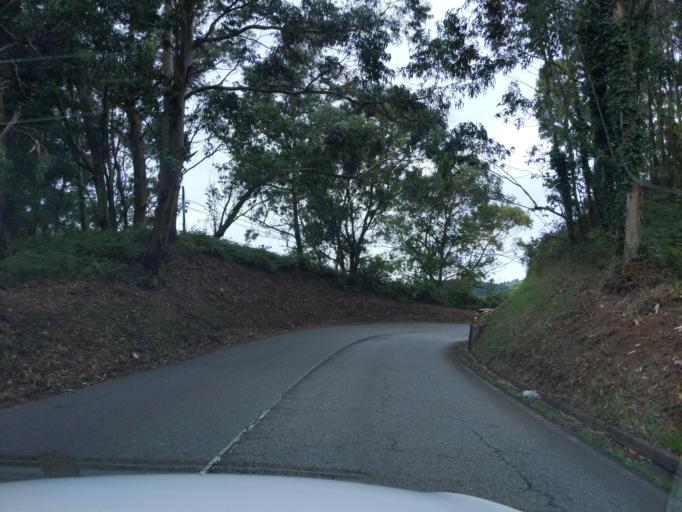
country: ES
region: Asturias
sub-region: Province of Asturias
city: Aviles
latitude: 43.5875
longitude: -5.9136
